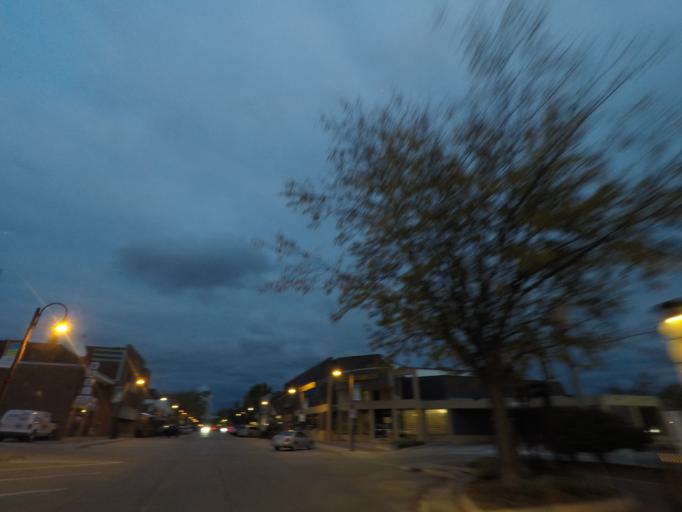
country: US
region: Iowa
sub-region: Story County
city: Ames
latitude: 42.0251
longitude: -93.6168
